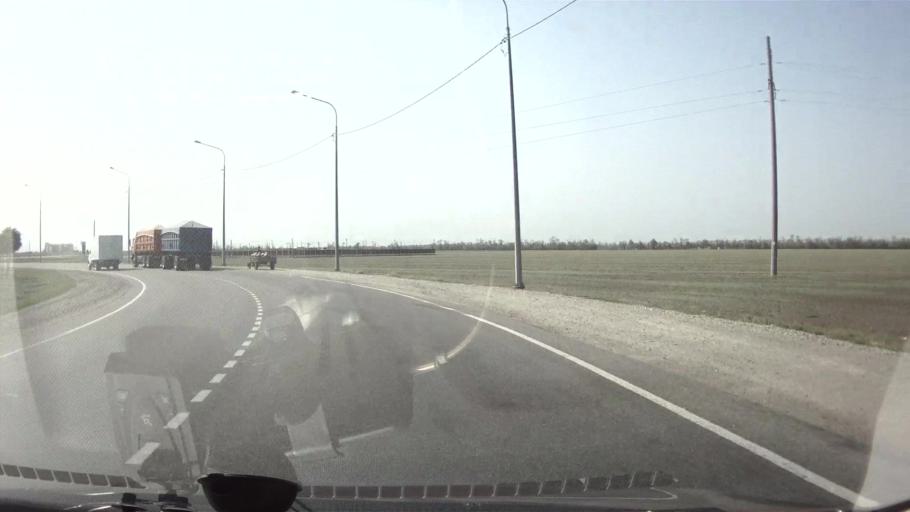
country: RU
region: Krasnodarskiy
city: Tbilisskaya
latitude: 45.3923
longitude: 40.1548
